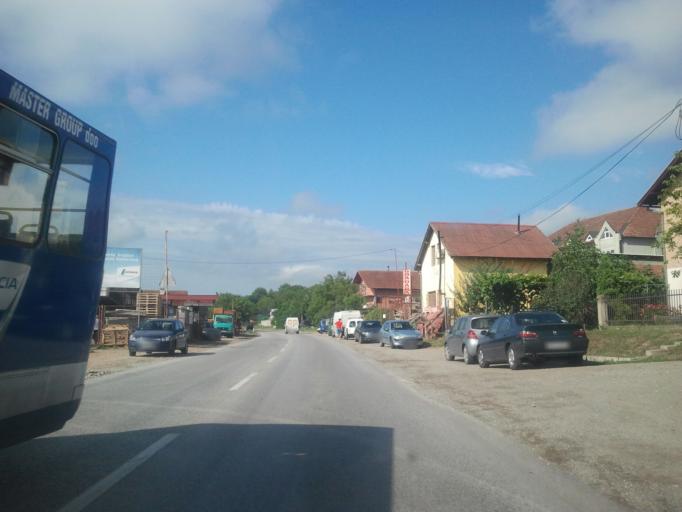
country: RS
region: Autonomna Pokrajina Vojvodina
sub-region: Juznobacki Okrug
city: Petrovaradin
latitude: 45.2292
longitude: 19.8821
